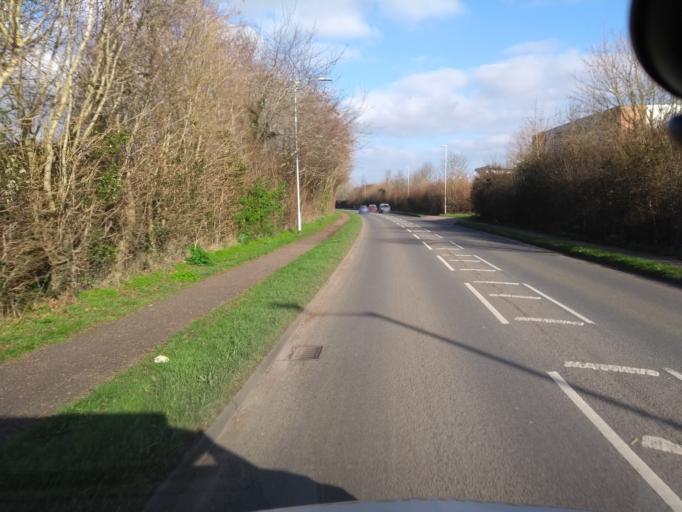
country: GB
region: England
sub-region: Somerset
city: Taunton
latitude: 51.0113
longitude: -3.0712
